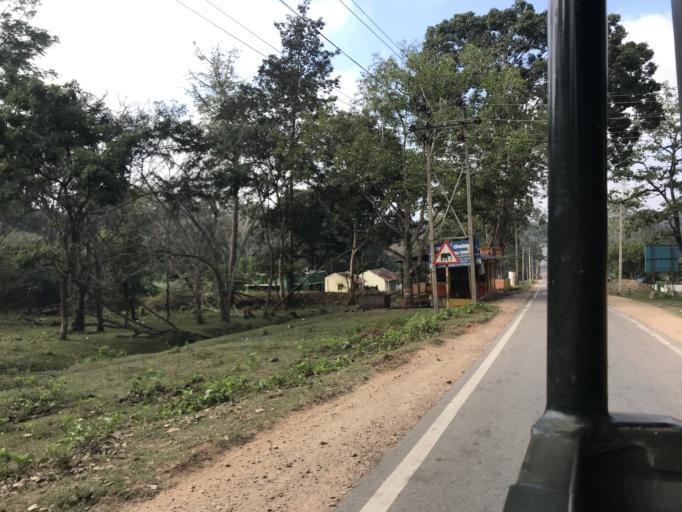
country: IN
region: Karnataka
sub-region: Mysore
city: Heggadadevankote
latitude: 11.9357
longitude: 76.1985
